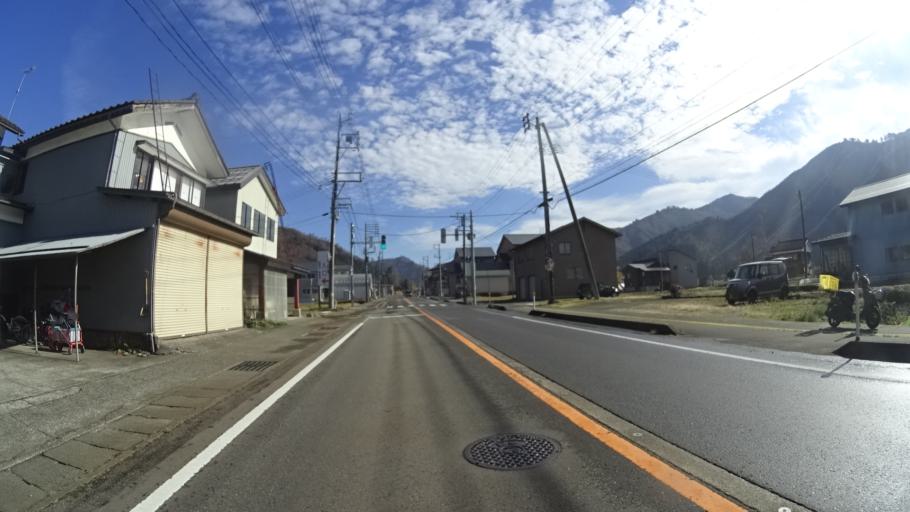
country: JP
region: Niigata
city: Muikamachi
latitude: 37.2268
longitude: 139.0025
